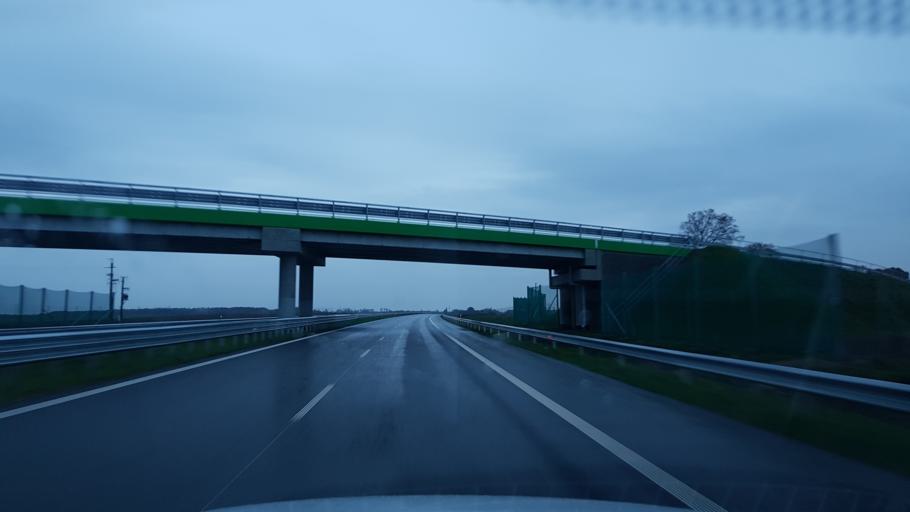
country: PL
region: West Pomeranian Voivodeship
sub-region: Powiat gryficki
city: Brojce
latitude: 53.9956
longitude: 15.4468
